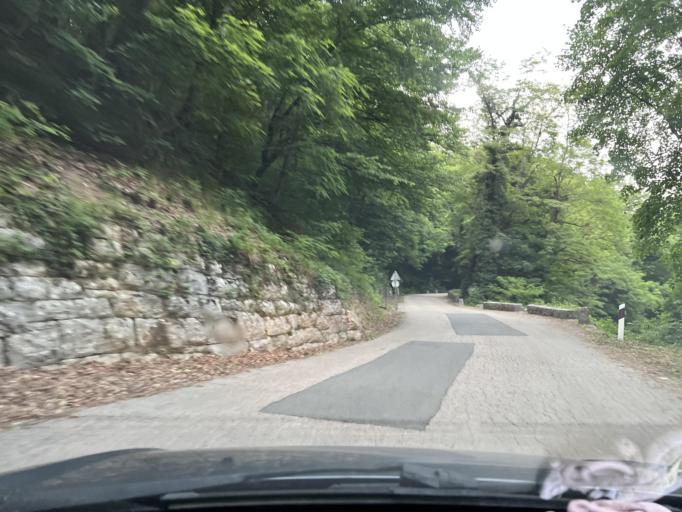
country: HR
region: Primorsko-Goranska
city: Marcelji
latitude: 45.3899
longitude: 14.4225
